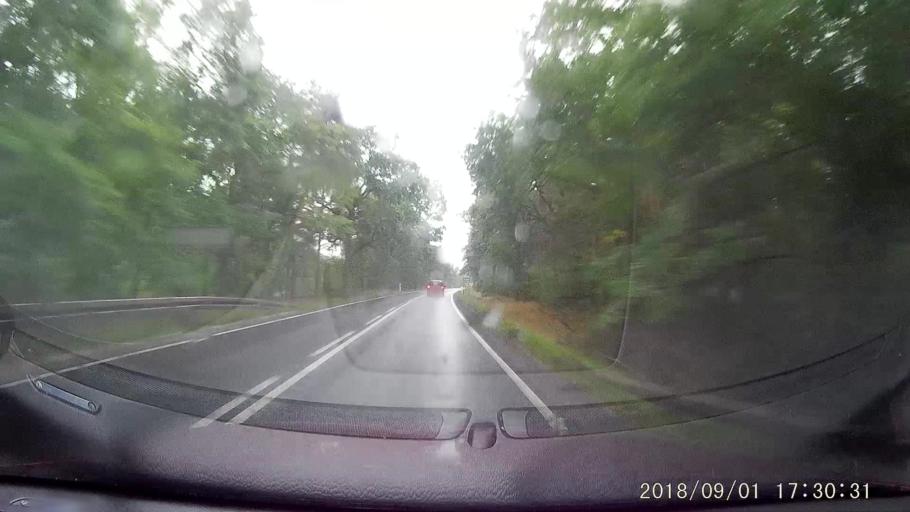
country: PL
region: Lubusz
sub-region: Powiat zaganski
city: Zagan
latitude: 51.6412
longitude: 15.3212
